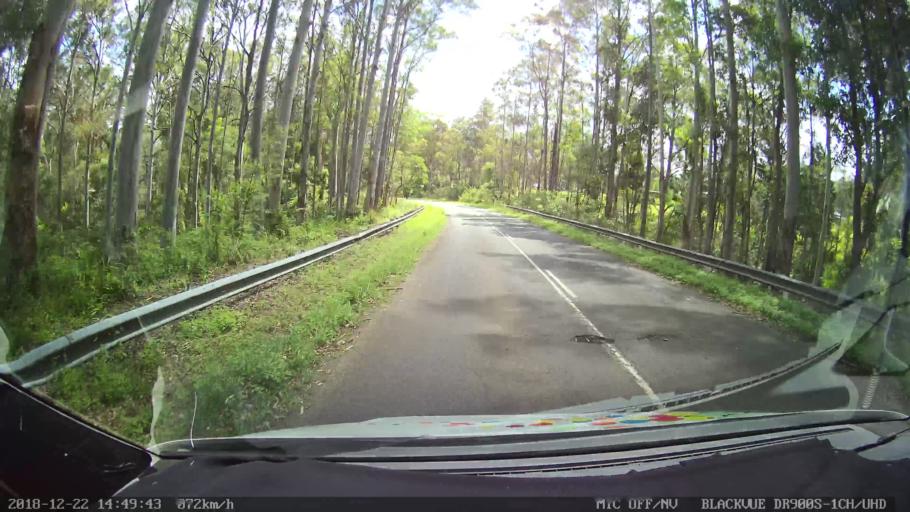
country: AU
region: New South Wales
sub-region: Bellingen
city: Dorrigo
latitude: -30.1897
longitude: 152.5440
